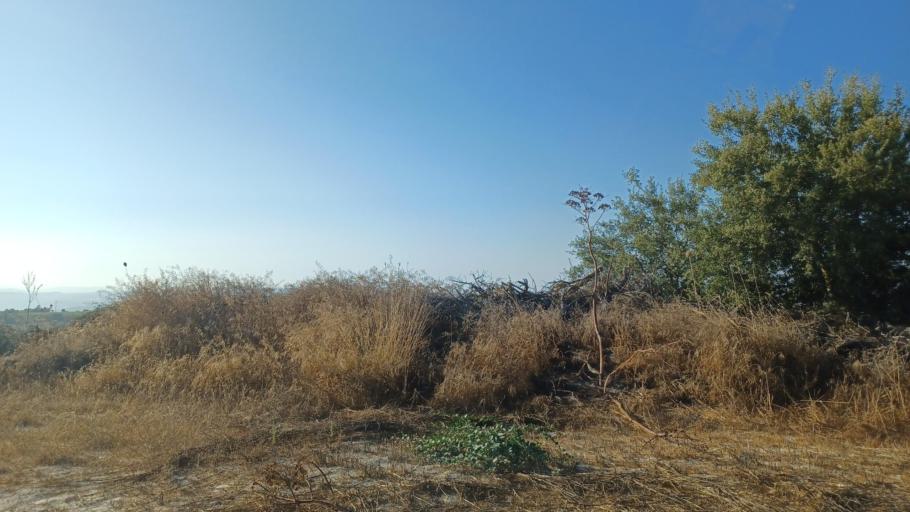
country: CY
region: Pafos
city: Mesogi
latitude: 34.8600
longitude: 32.5148
